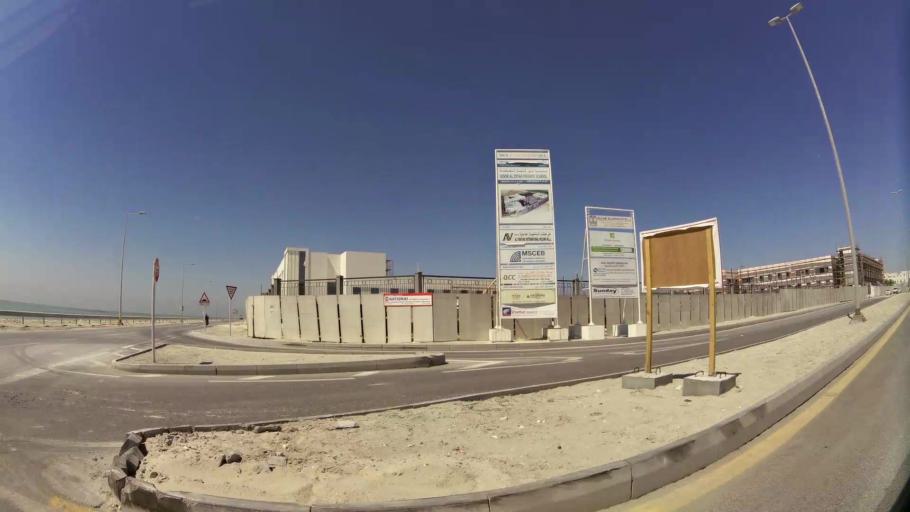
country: BH
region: Muharraq
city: Al Muharraq
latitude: 26.2979
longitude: 50.6366
